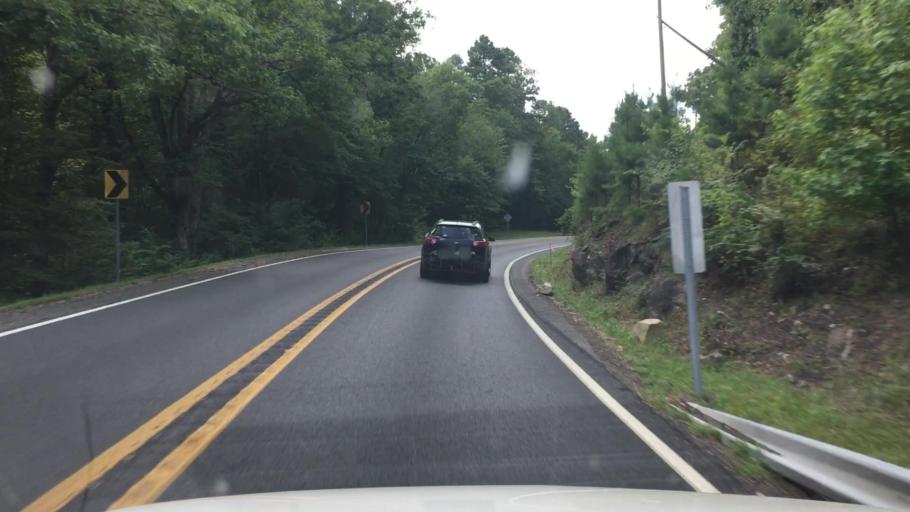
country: US
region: Arkansas
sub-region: Garland County
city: Lake Hamilton
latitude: 34.3437
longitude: -93.1839
